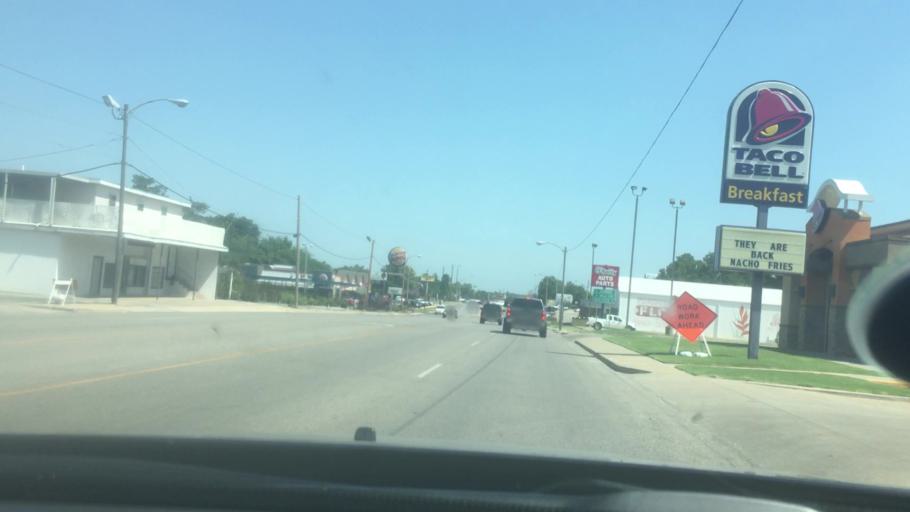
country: US
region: Oklahoma
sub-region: Pontotoc County
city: Ada
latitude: 34.7789
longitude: -96.6699
